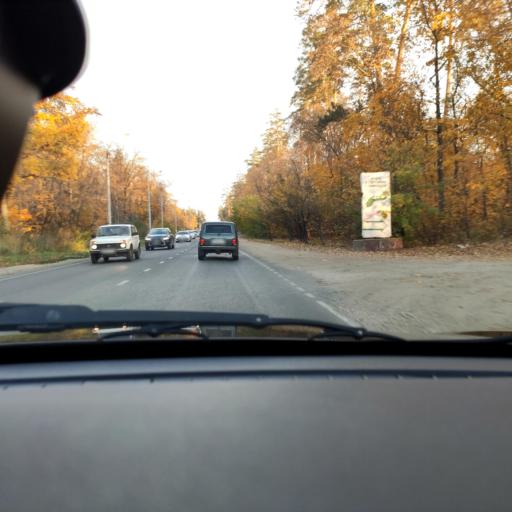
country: RU
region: Samara
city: Tol'yatti
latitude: 53.4933
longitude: 49.2962
